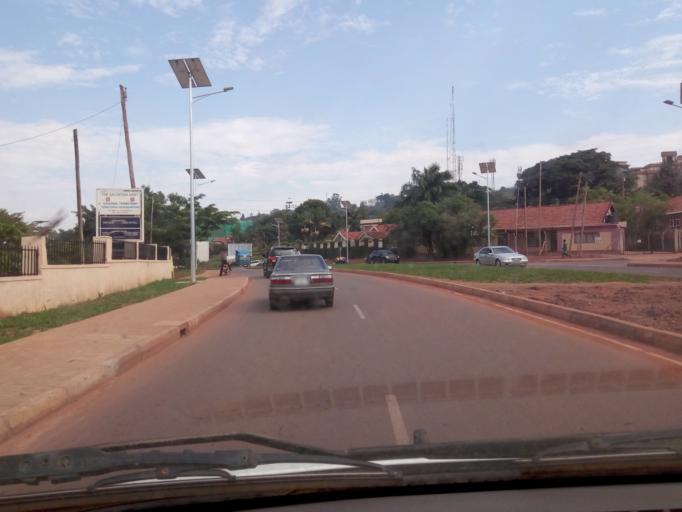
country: UG
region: Central Region
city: Kampala Central Division
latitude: 0.3426
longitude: 32.5955
